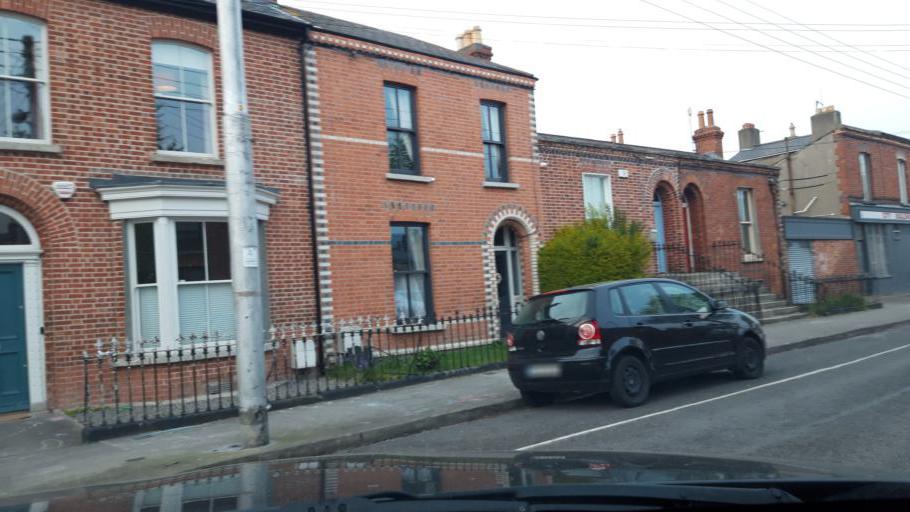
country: IE
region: Leinster
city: Rathmines
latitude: 53.3336
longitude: -6.2703
